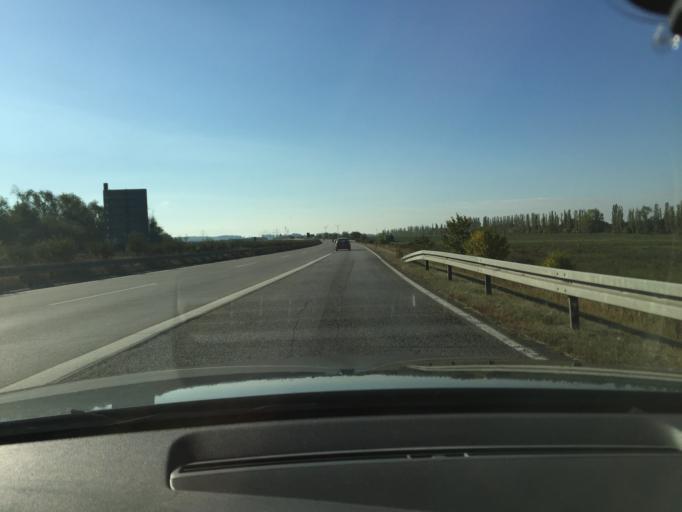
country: DE
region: Mecklenburg-Vorpommern
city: Roggentin
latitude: 54.0770
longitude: 12.1947
